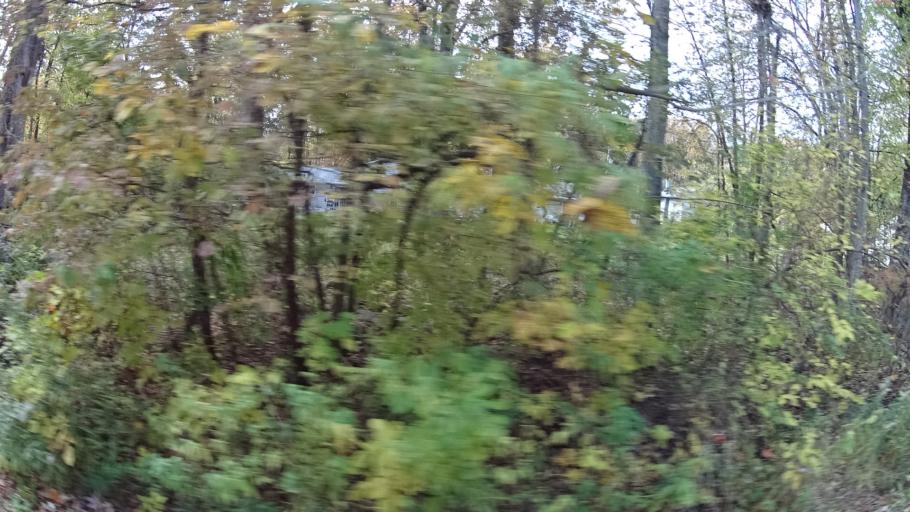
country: US
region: Ohio
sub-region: Lorain County
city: Sheffield Lake
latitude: 41.4829
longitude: -82.0967
